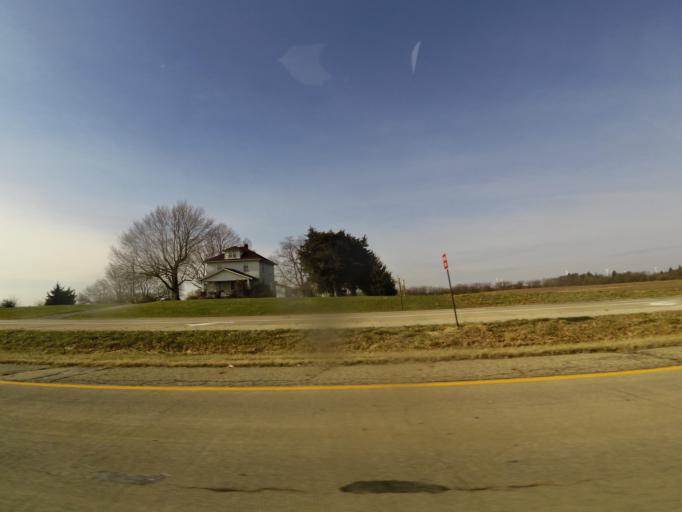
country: US
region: Illinois
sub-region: Macon County
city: Forsyth
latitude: 39.9575
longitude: -88.9555
